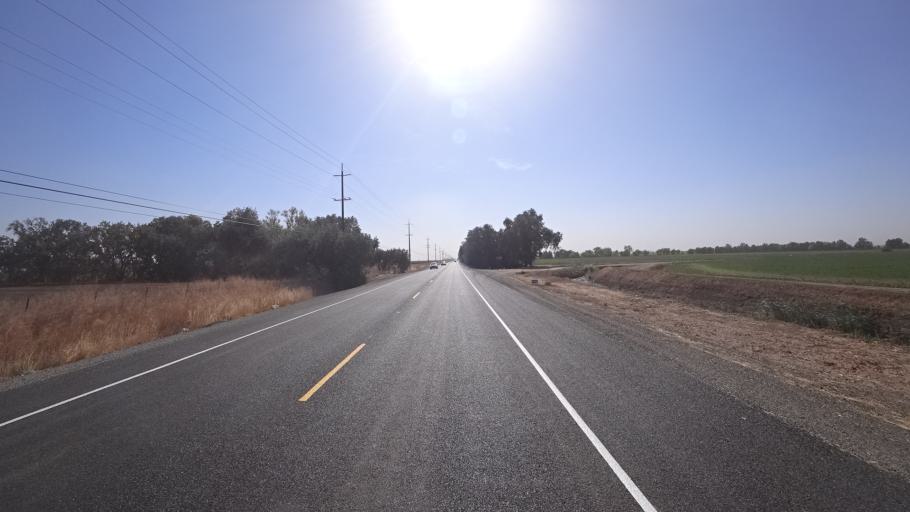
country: US
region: California
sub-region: Yolo County
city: Woodland
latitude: 38.6308
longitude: -121.7292
